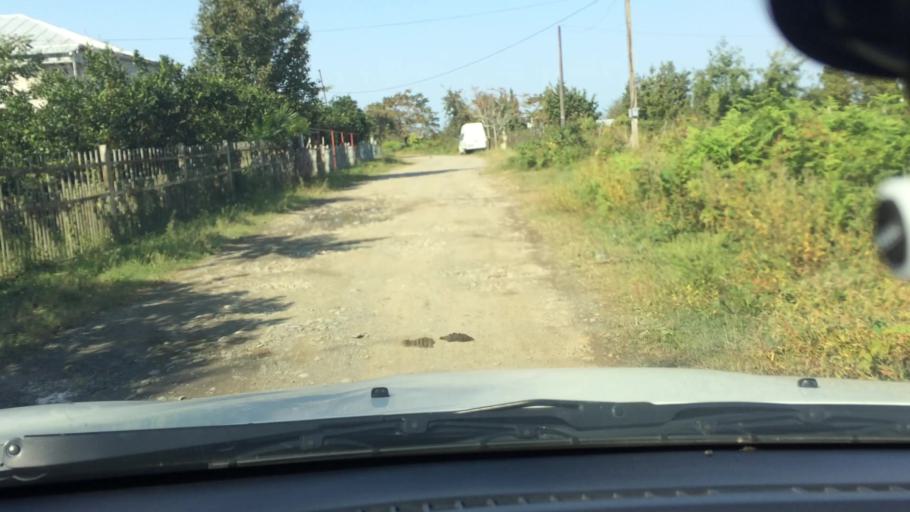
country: GE
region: Ajaria
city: Kobuleti
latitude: 41.8094
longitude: 41.8207
